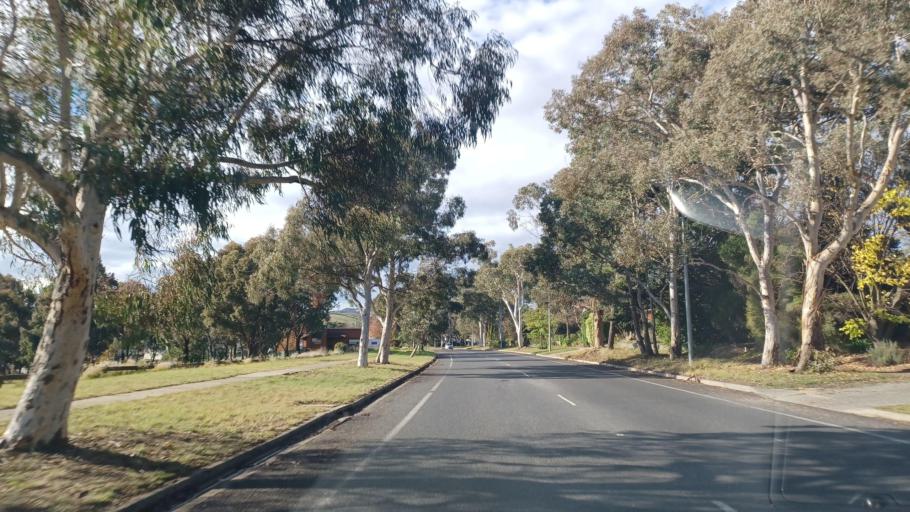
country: AU
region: Australian Capital Territory
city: Belconnen
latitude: -35.1914
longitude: 149.0448
